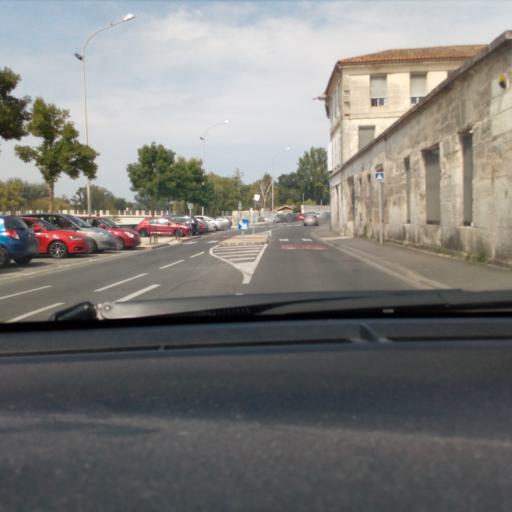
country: FR
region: Poitou-Charentes
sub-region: Departement de la Charente
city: Angouleme
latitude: 45.6581
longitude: 0.1605
